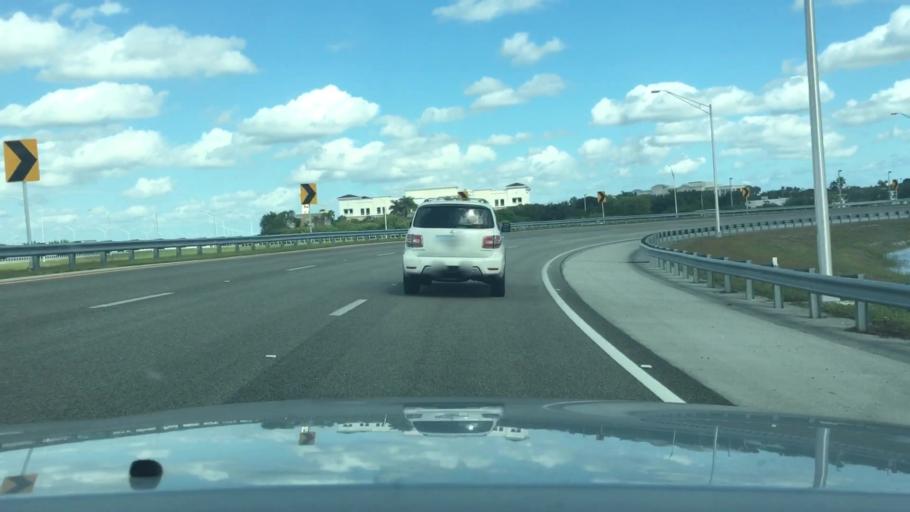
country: US
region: Florida
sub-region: Miami-Dade County
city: Country Club
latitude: 25.9800
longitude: -80.3502
